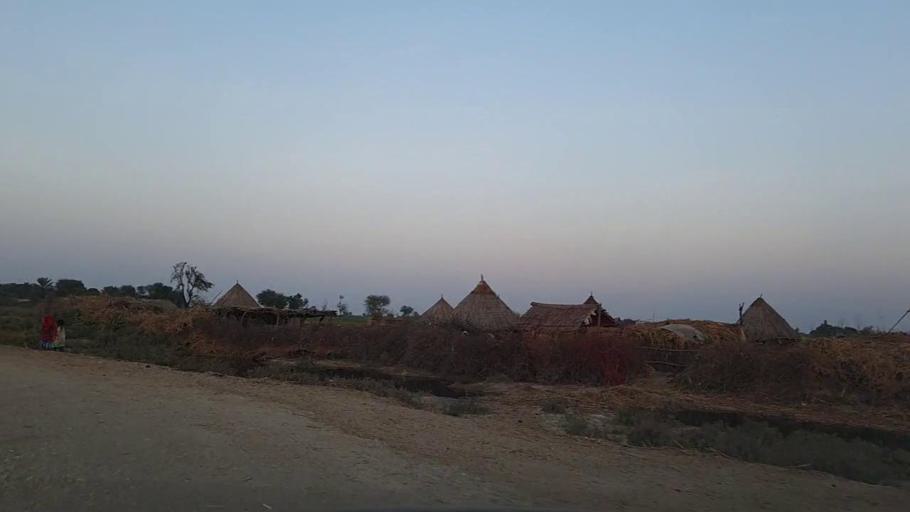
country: PK
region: Sindh
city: Tando Mittha Khan
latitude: 25.9402
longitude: 69.1445
